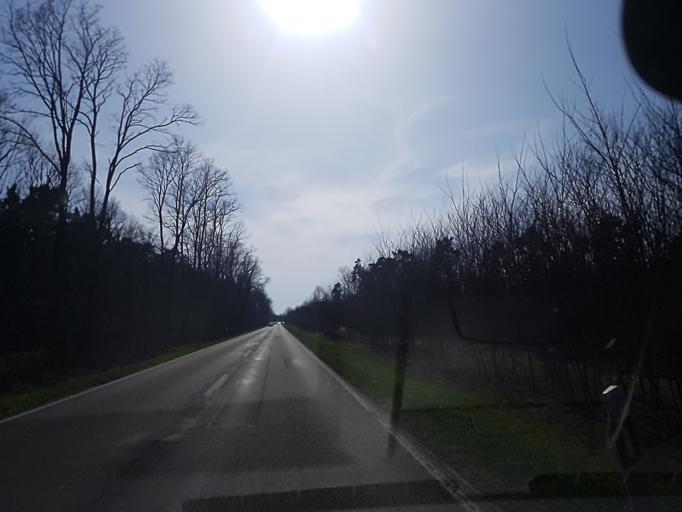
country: DE
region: Brandenburg
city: Vetschau
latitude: 51.7673
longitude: 14.0159
